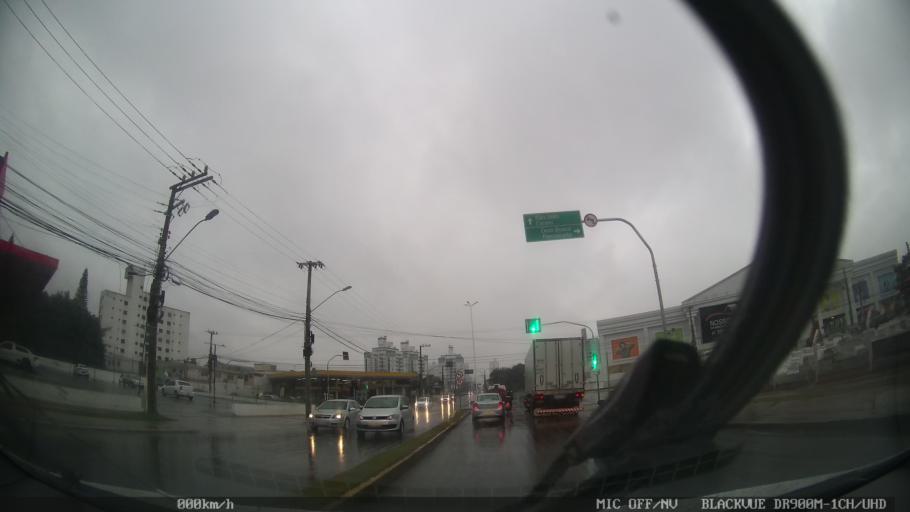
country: BR
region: Santa Catarina
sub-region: Itajai
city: Itajai
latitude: -26.9102
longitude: -48.6834
